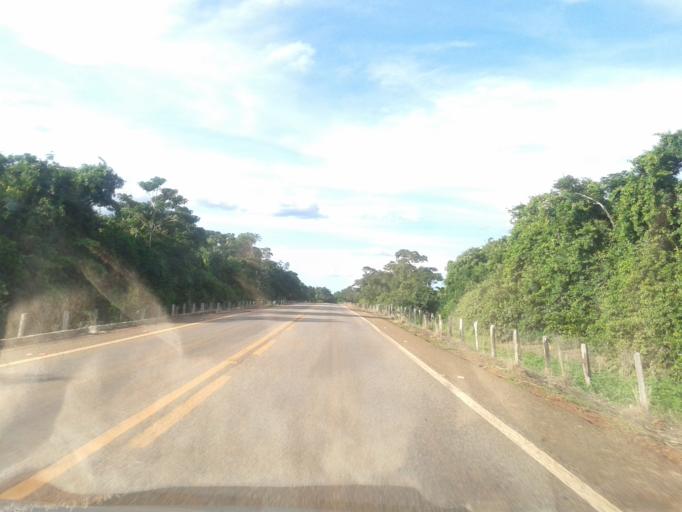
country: BR
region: Goias
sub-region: Crixas
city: Crixas
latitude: -14.0327
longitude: -50.3281
